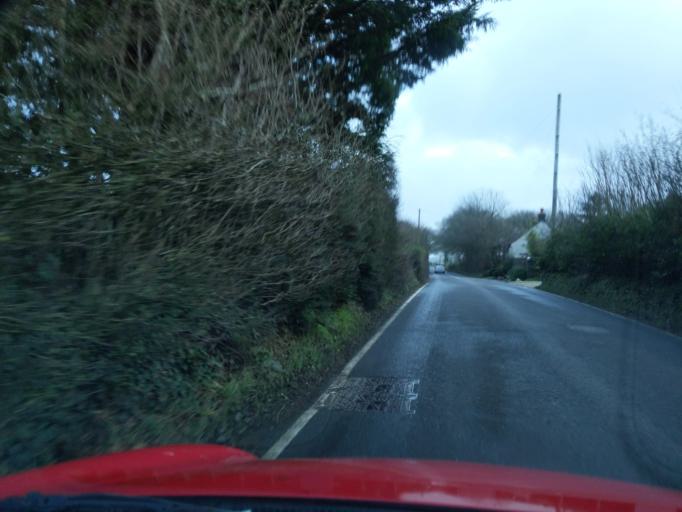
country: GB
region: England
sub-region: Devon
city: Holsworthy
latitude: 50.8820
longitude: -4.2891
